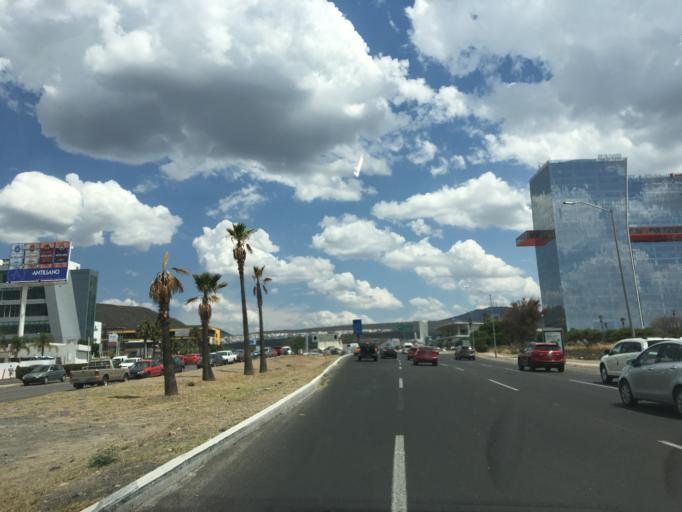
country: MX
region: Queretaro
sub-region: Queretaro
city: Santiago de Queretaro
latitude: 20.5759
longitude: -100.3609
